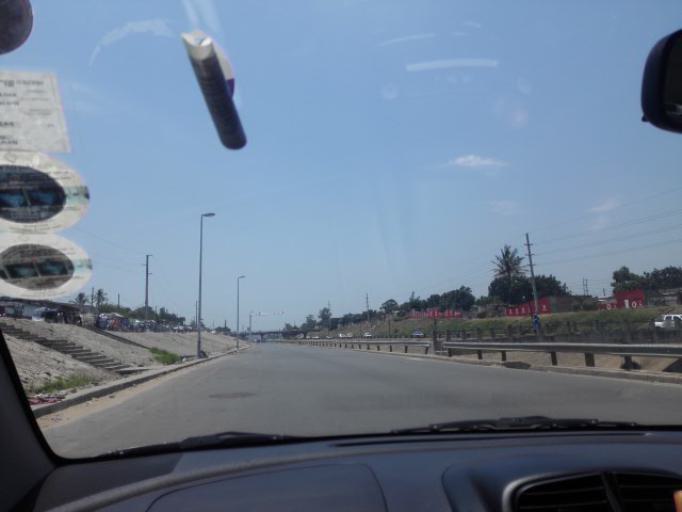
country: MZ
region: Maputo City
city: Maputo
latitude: -25.9305
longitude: 32.5587
